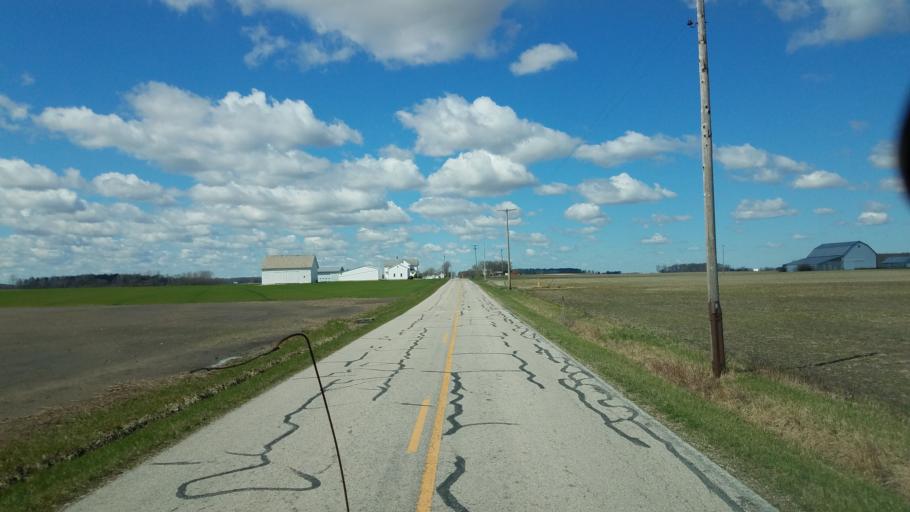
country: US
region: Ohio
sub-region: Sandusky County
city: Mount Carmel
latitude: 41.2416
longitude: -82.9451
